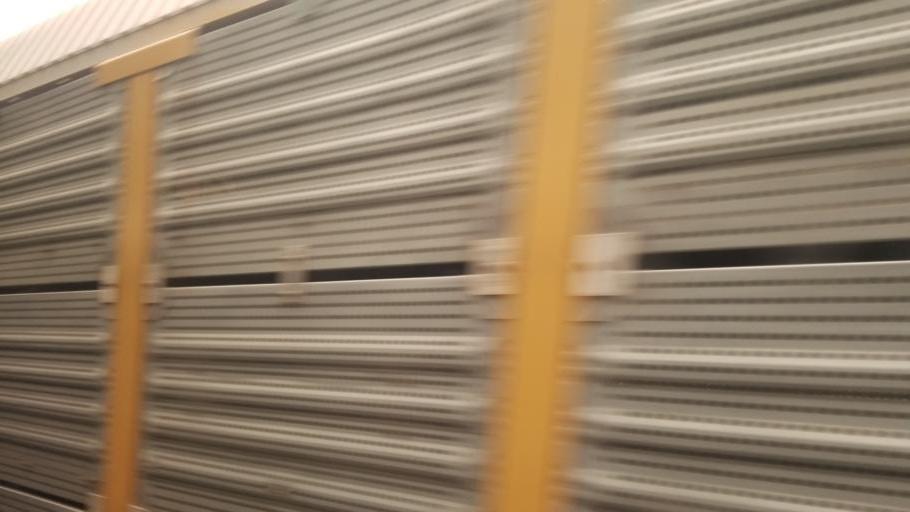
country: US
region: Pennsylvania
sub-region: Somerset County
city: Milford
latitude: 39.8802
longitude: -79.1118
